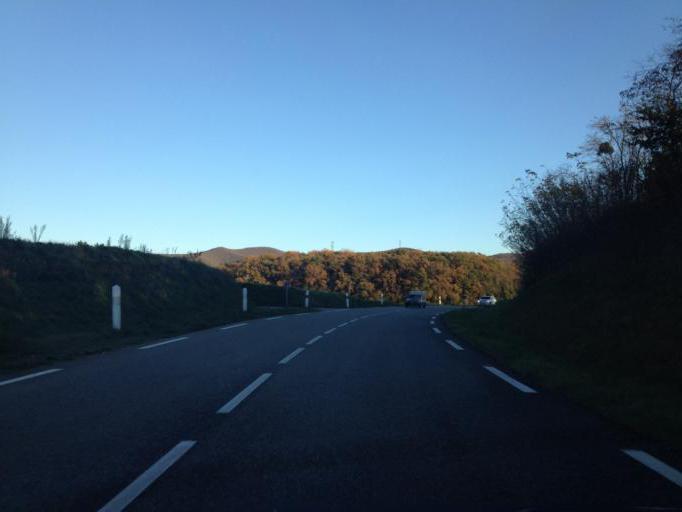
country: FR
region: Rhone-Alpes
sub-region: Departement de l'Ardeche
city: Chomerac
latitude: 44.6995
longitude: 4.7055
